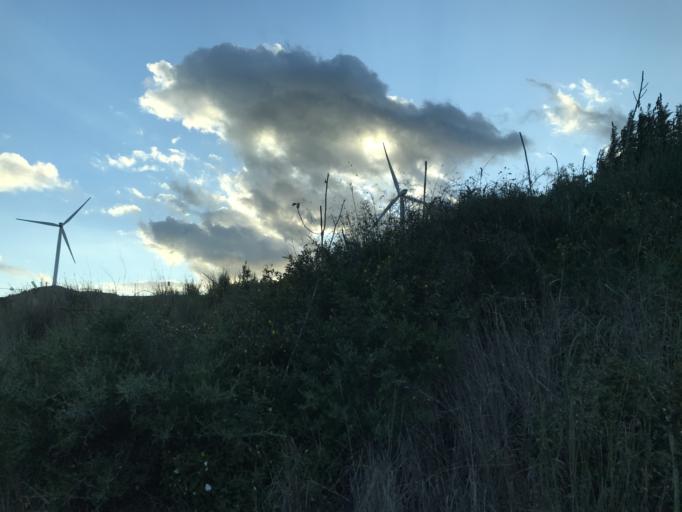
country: TR
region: Hatay
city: Buyukcat
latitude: 36.1089
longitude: 36.0480
